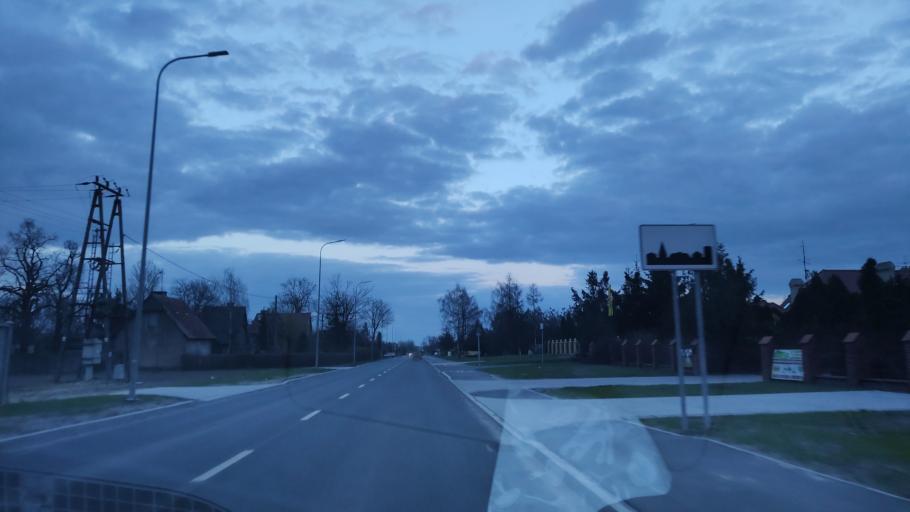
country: PL
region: Kujawsko-Pomorskie
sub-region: Powiat zninski
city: Znin
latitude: 52.8497
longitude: 17.7023
